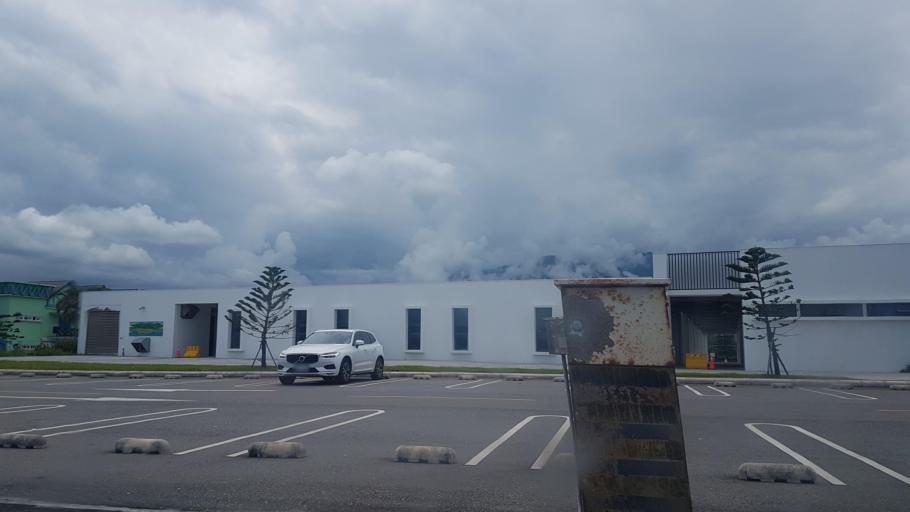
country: TW
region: Taiwan
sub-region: Hualien
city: Hualian
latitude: 23.9991
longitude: 121.6420
